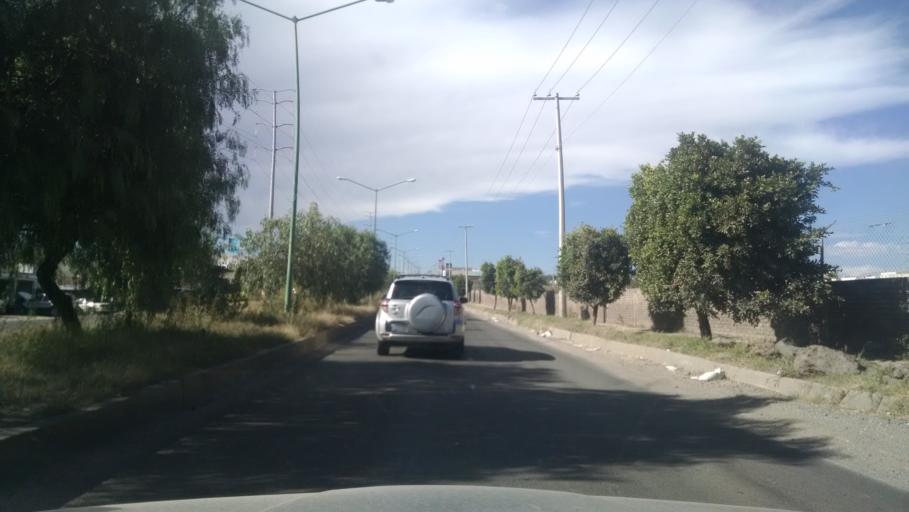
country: MX
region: Guanajuato
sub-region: Leon
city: La Ermita
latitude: 21.1486
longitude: -101.7281
